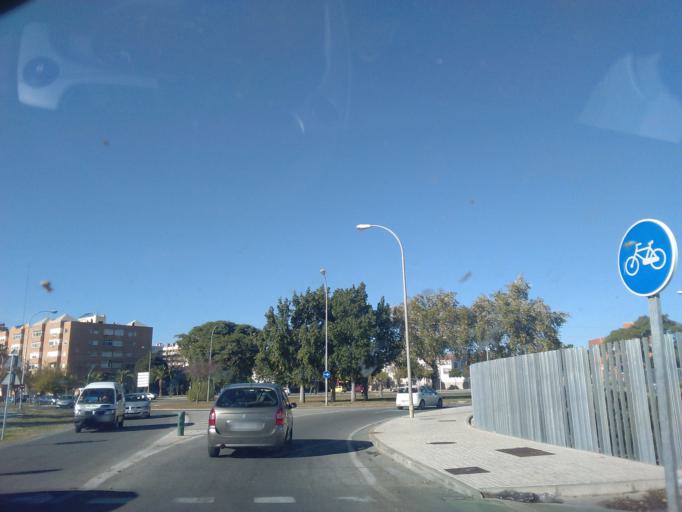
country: ES
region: Andalusia
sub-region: Provincia de Sevilla
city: Sevilla
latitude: 37.3862
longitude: -5.9166
